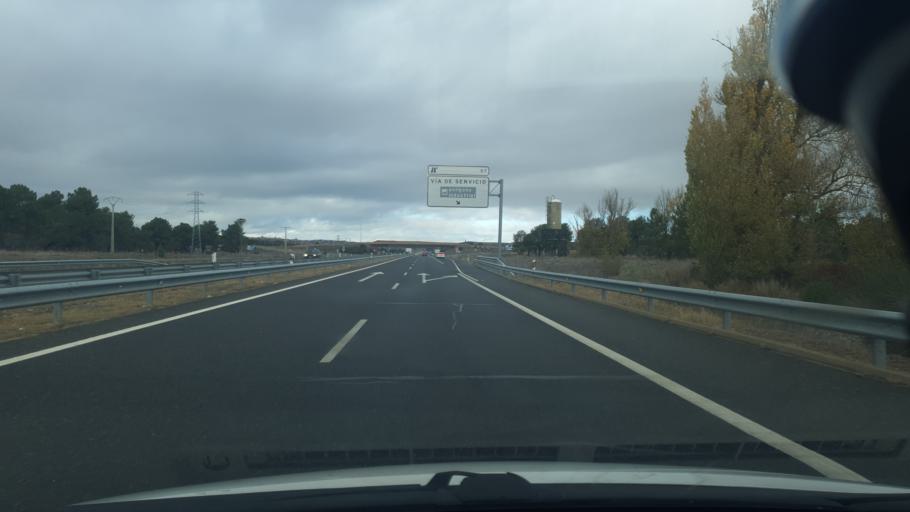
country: ES
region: Castille and Leon
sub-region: Provincia de Segovia
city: Cuellar
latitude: 41.3651
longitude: -4.2985
